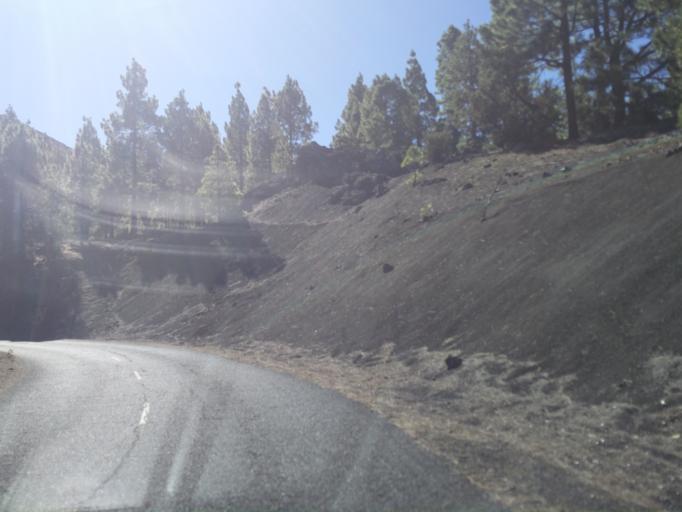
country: ES
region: Canary Islands
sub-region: Provincia de Santa Cruz de Tenerife
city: El Paso
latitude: 28.6170
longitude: -17.8460
